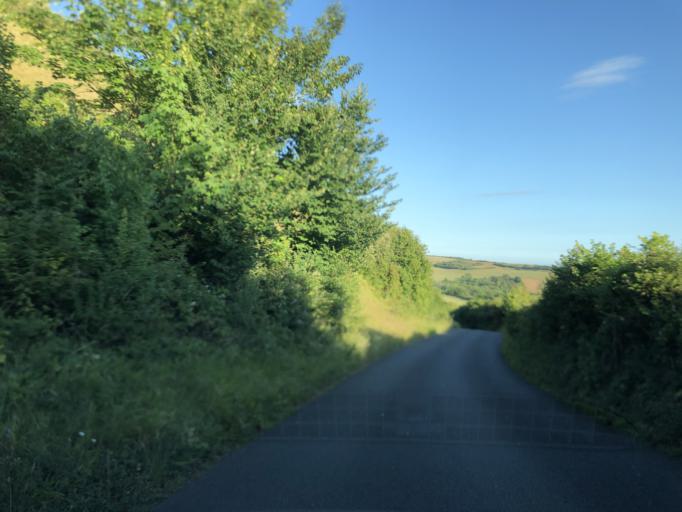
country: GB
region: England
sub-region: Isle of Wight
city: Shalfleet
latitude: 50.6574
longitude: -1.4027
